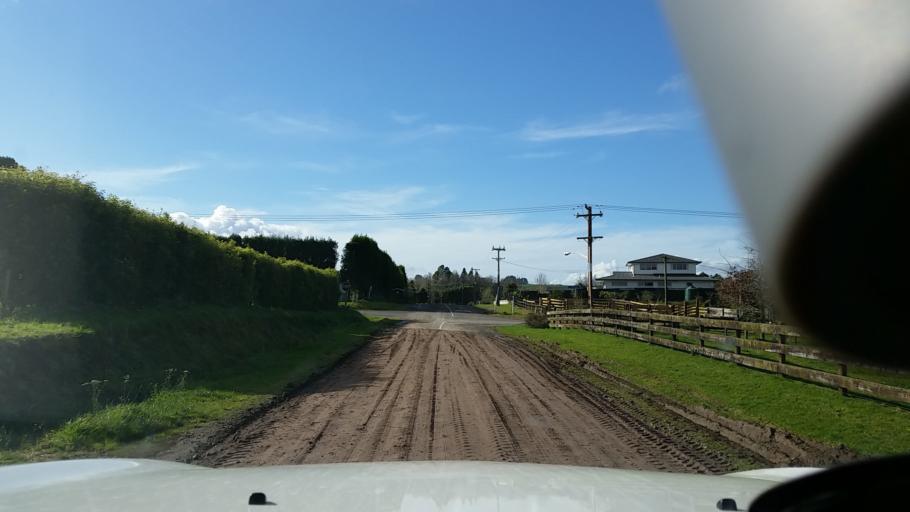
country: NZ
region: Bay of Plenty
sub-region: Rotorua District
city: Rotorua
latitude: -38.0358
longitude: 176.1976
